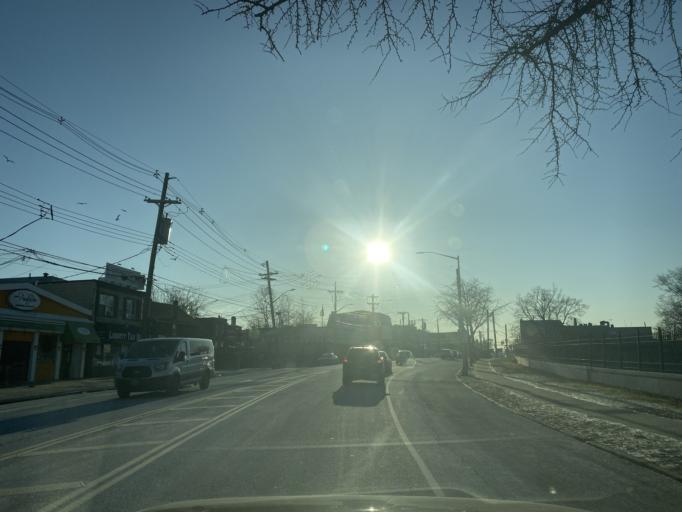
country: US
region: New York
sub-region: Bronx
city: The Bronx
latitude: 40.8345
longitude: -73.8295
